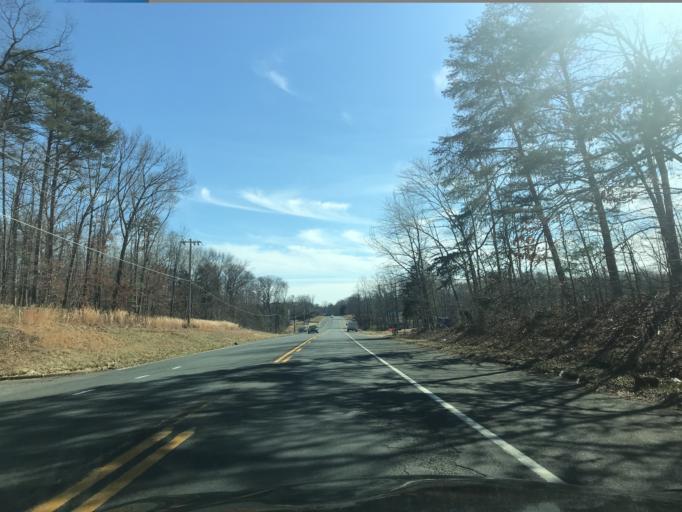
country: US
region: Maryland
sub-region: Charles County
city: Bryans Road
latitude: 38.6470
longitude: -77.0743
